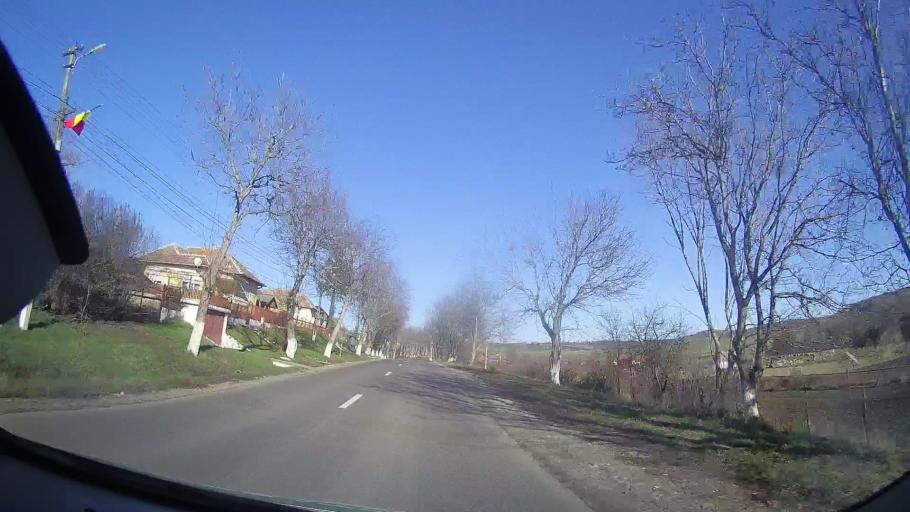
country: RO
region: Mures
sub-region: Comuna Sarmasu
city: Balda
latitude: 46.7334
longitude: 24.1474
